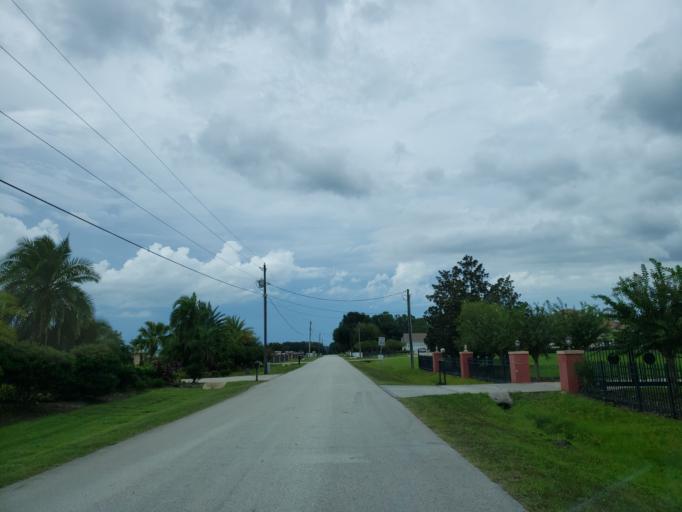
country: US
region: Florida
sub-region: Polk County
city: Willow Oak
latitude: 27.9532
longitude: -82.0513
